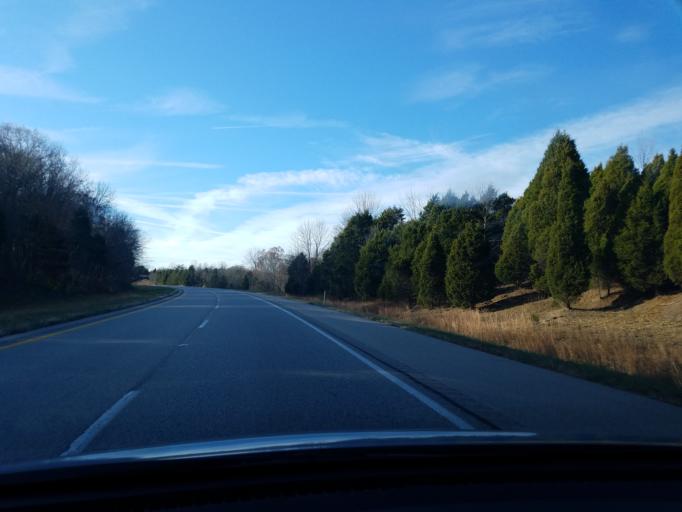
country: US
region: Indiana
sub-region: Harrison County
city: Corydon
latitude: 38.2539
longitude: -86.2795
